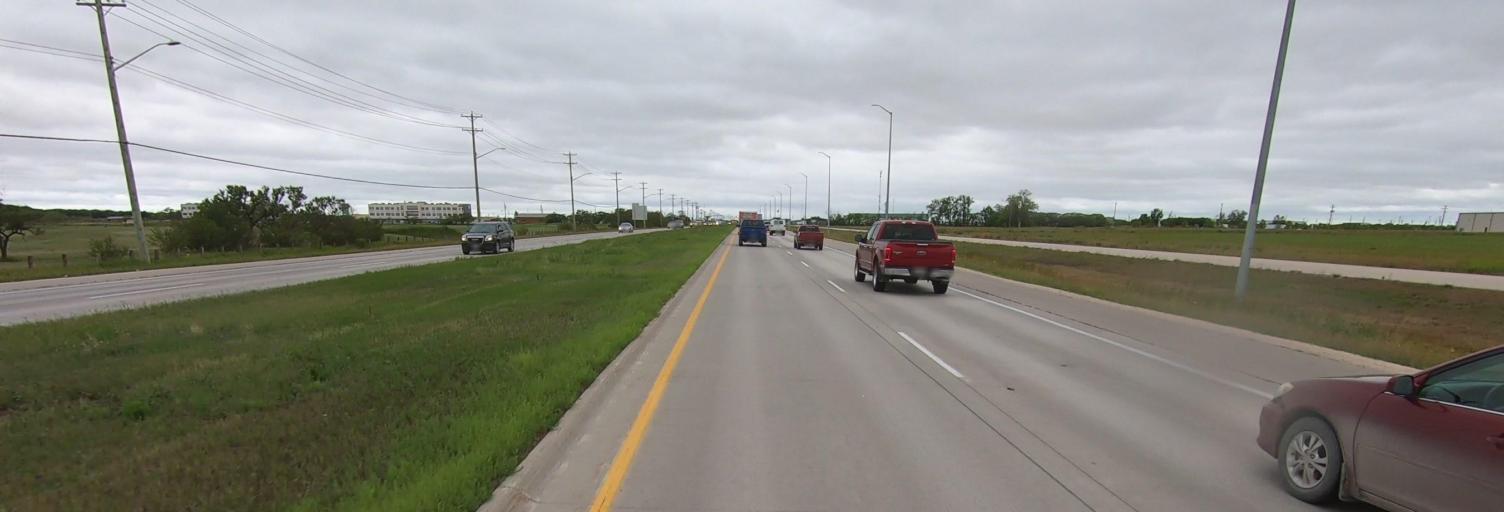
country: CA
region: Manitoba
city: Headingley
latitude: 49.8761
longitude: -97.3672
